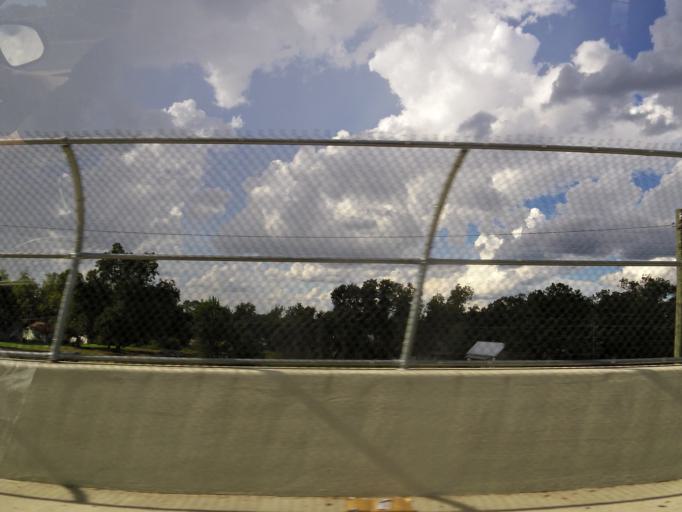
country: US
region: Georgia
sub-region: Lowndes County
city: Valdosta
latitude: 30.8268
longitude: -83.2893
